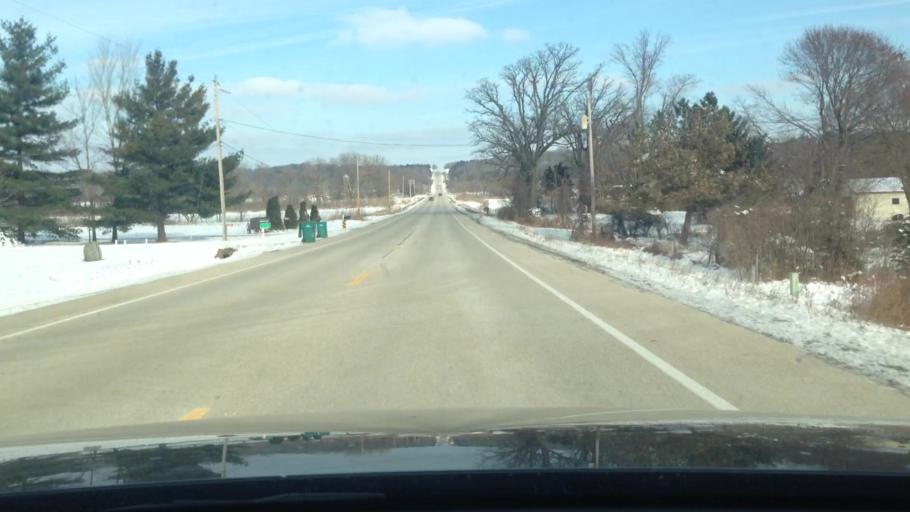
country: US
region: Wisconsin
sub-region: Walworth County
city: East Troy
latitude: 42.7220
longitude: -88.4055
